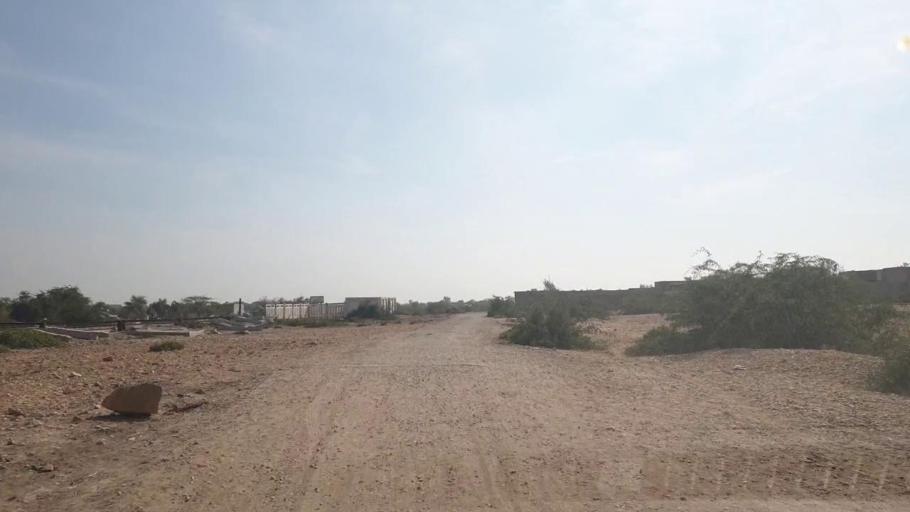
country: PK
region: Sindh
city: Hala
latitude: 25.7488
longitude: 68.2940
